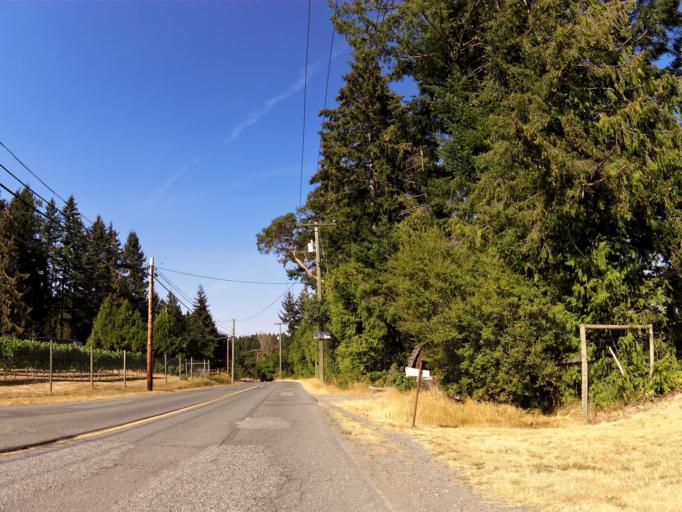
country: CA
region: British Columbia
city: North Saanich
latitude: 48.6777
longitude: -123.5507
